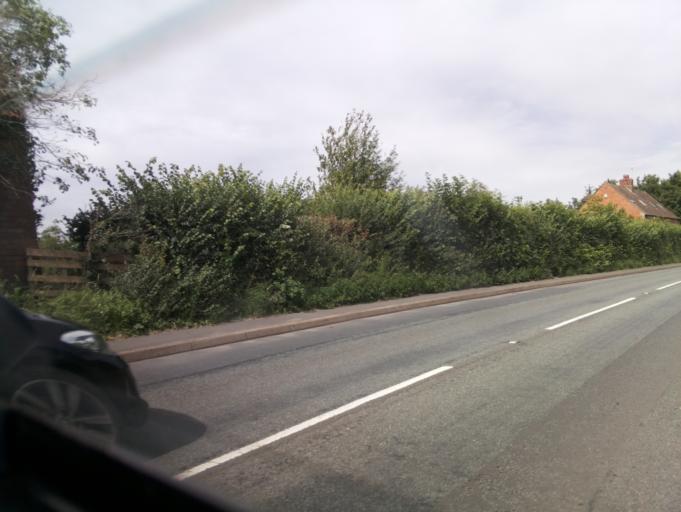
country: GB
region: England
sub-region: Somerset
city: Wells
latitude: 51.1960
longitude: -2.6670
